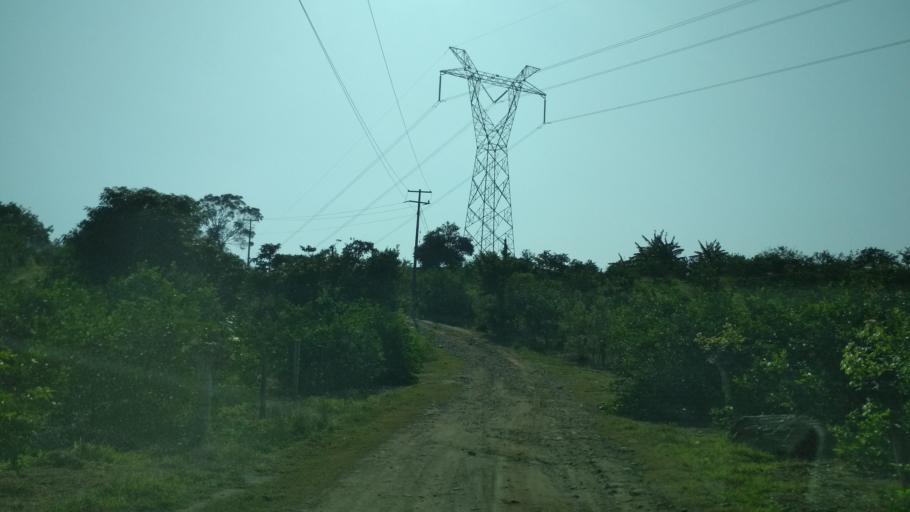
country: MX
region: Puebla
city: San Jose Acateno
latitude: 20.1707
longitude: -97.1736
